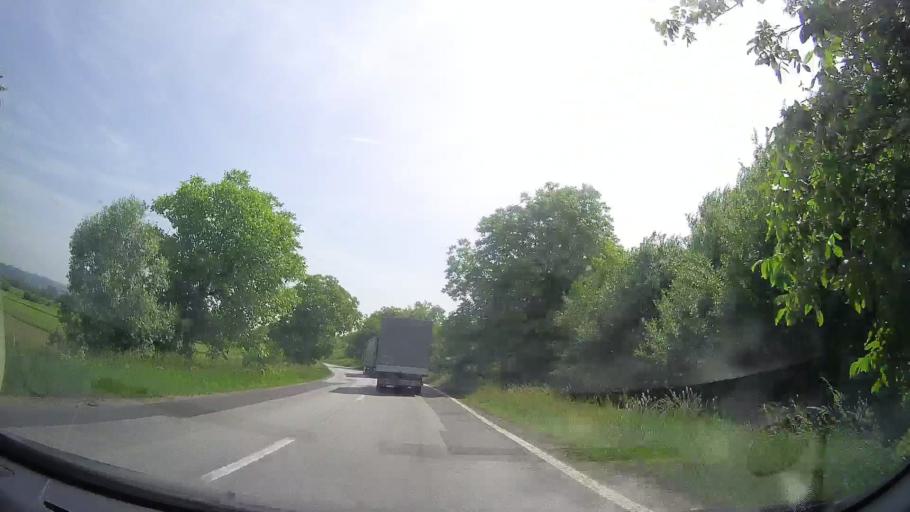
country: RO
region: Hunedoara
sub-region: Comuna Dobra
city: Dobra
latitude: 45.9081
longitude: 22.5886
